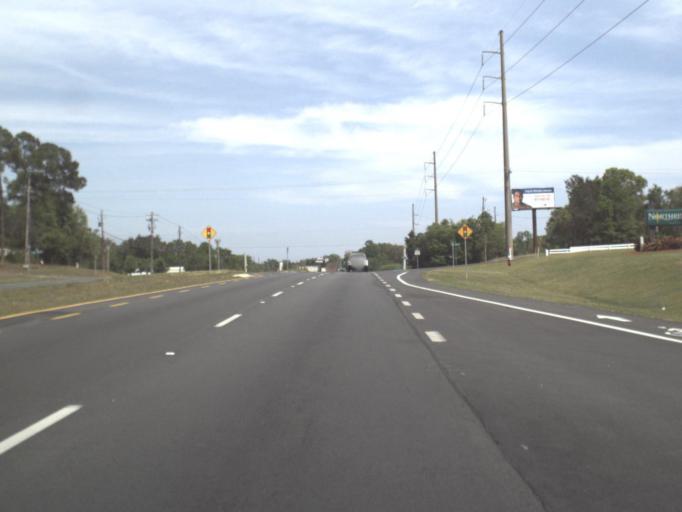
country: US
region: Florida
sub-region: Escambia County
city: Ferry Pass
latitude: 30.5319
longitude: -87.2174
